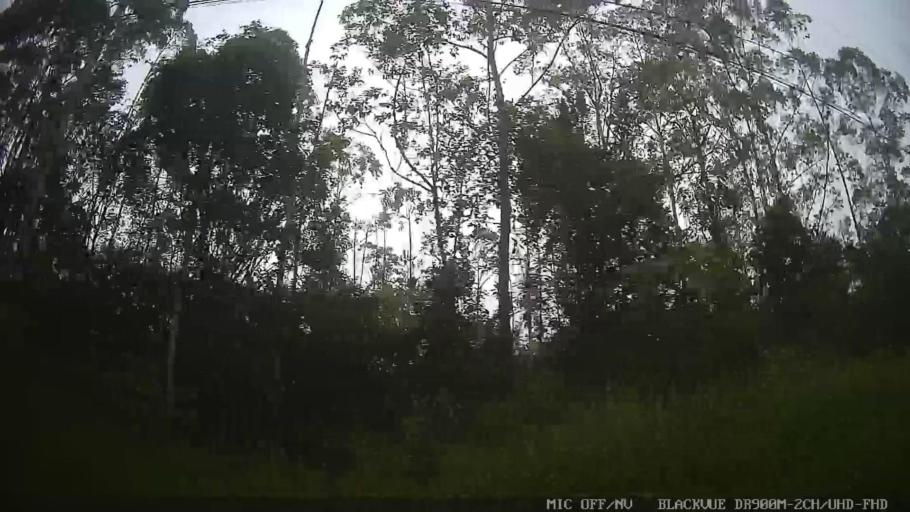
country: BR
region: Sao Paulo
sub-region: Suzano
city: Suzano
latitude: -23.6668
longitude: -46.2372
